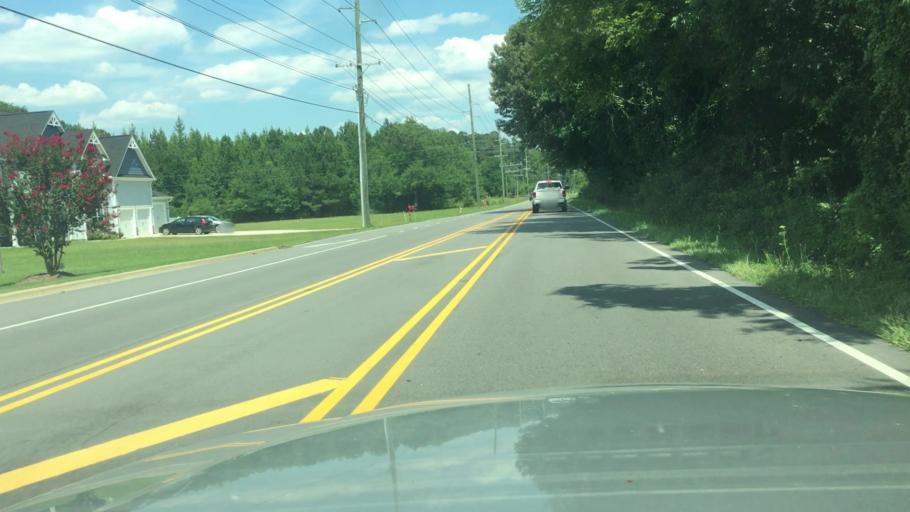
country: US
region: North Carolina
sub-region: Cumberland County
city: Hope Mills
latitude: 34.9497
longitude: -78.8538
